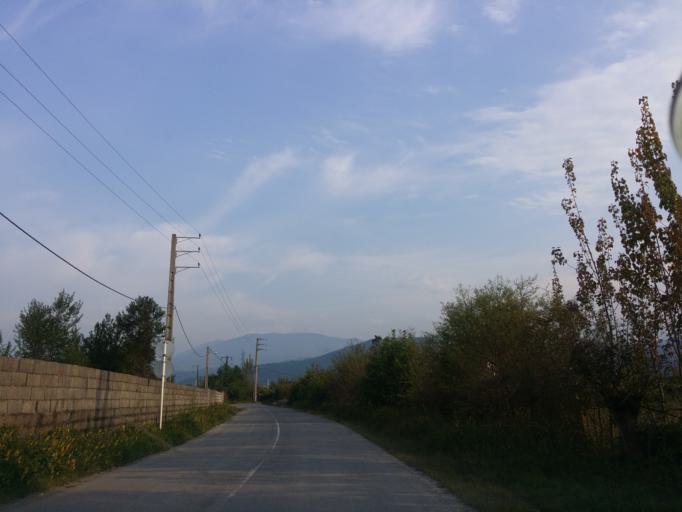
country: IR
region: Mazandaran
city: Chalus
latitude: 36.6780
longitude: 51.3726
